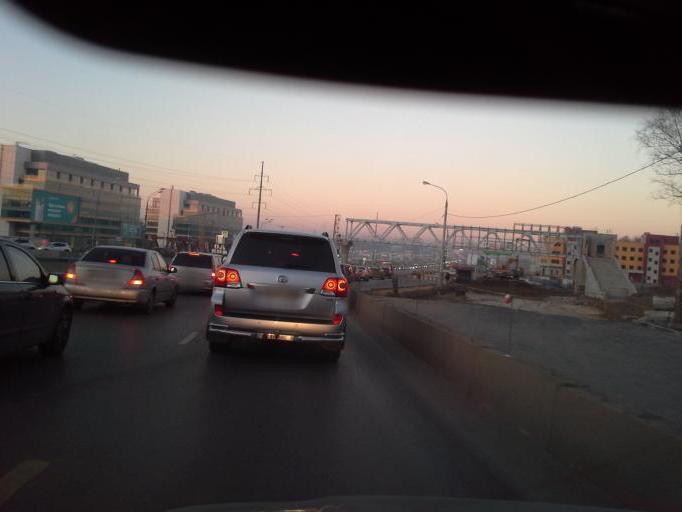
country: RU
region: Moskovskaya
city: Kommunarka
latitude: 55.5875
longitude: 37.4741
